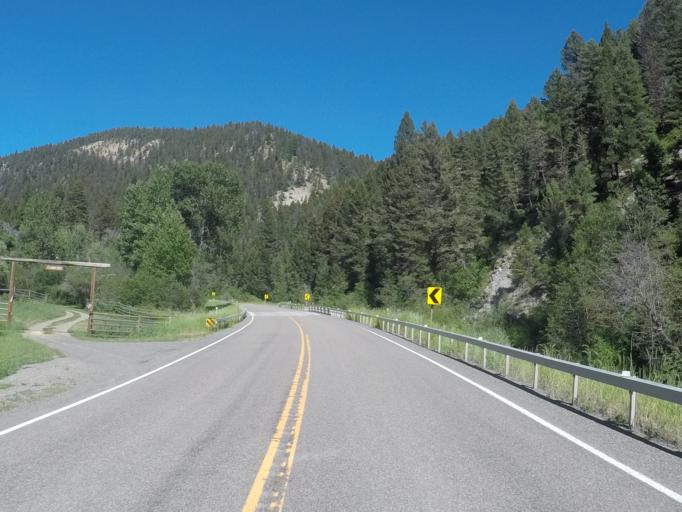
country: US
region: Montana
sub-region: Meagher County
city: White Sulphur Springs
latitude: 46.3482
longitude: -111.1368
